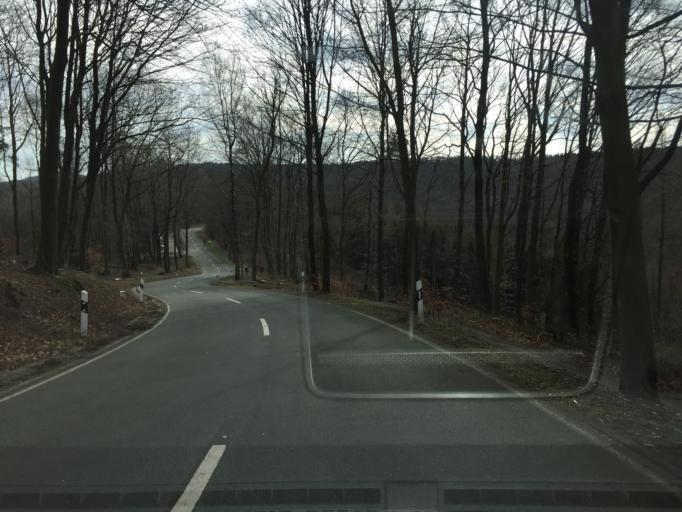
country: DE
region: North Rhine-Westphalia
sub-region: Regierungsbezirk Detmold
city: Detmold
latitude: 51.9087
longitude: 8.8395
